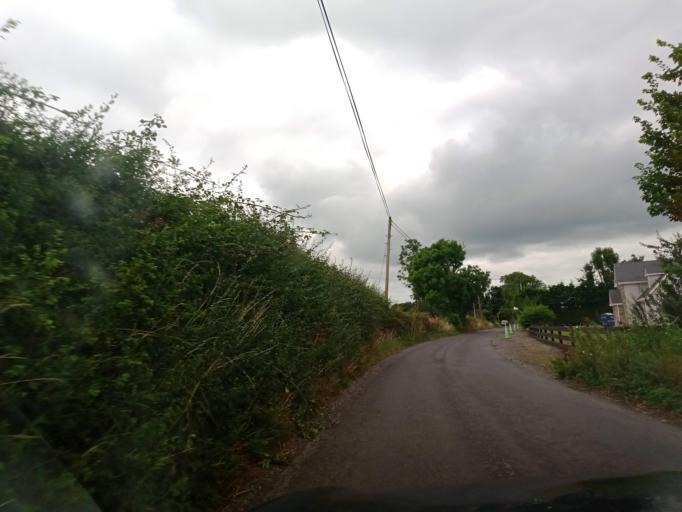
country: IE
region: Leinster
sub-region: Laois
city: Stradbally
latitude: 52.9836
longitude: -7.1678
